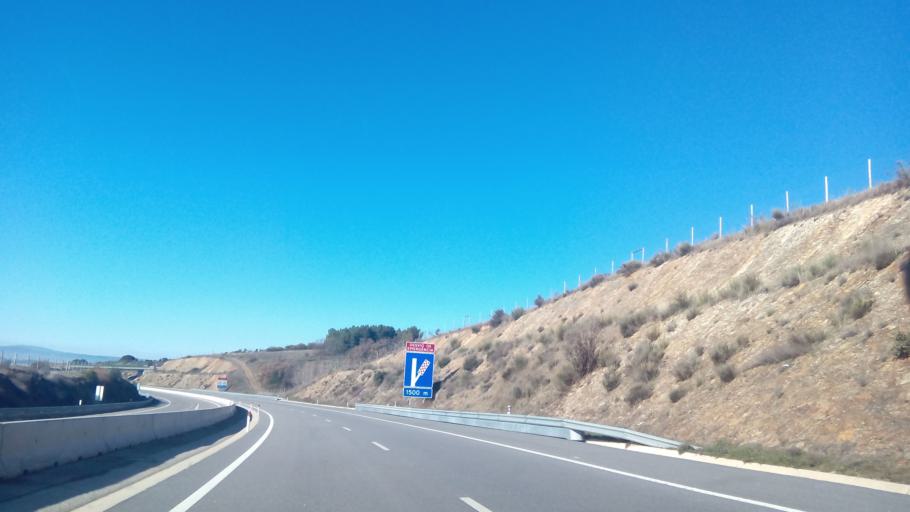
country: PT
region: Braganca
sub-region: Braganca Municipality
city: Braganca
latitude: 41.7521
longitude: -6.6307
